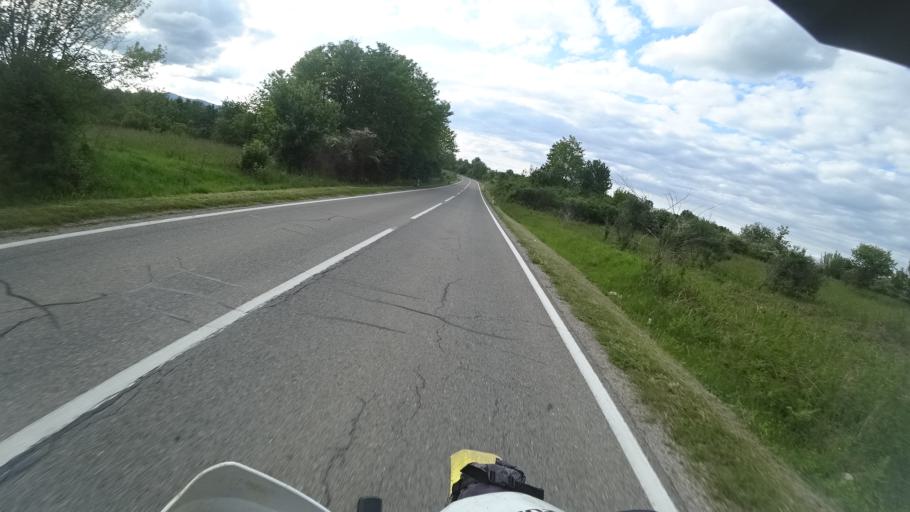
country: HR
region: Licko-Senjska
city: Gospic
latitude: 44.5116
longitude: 15.4273
